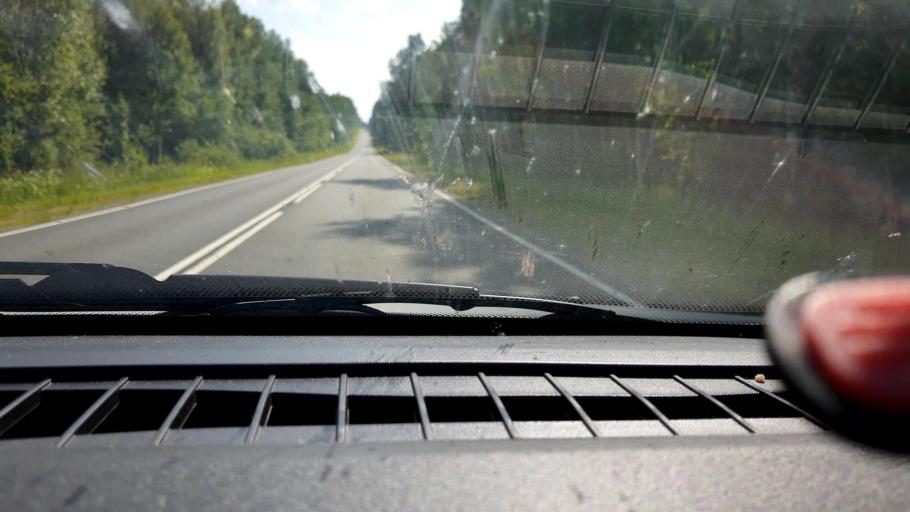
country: RU
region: Nizjnij Novgorod
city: Uren'
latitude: 57.2696
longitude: 45.6253
